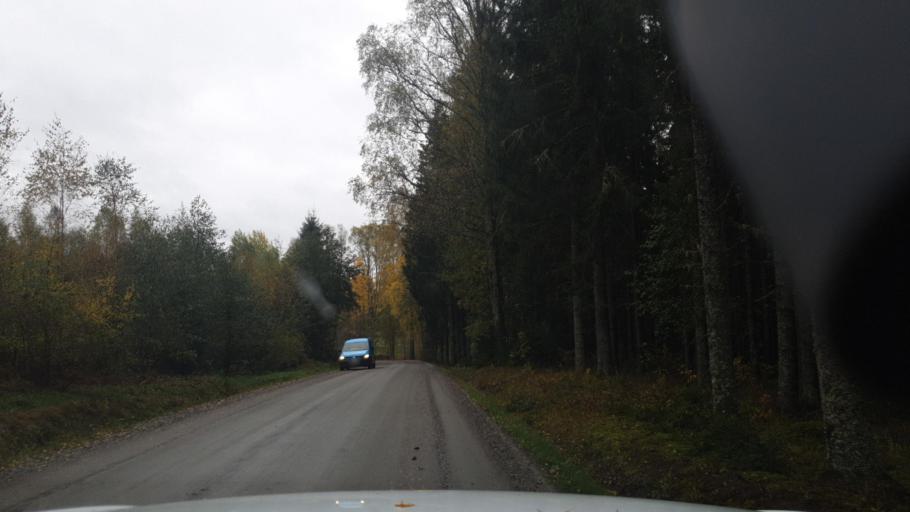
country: SE
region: Vaermland
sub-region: Karlstads Kommun
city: Edsvalla
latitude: 59.4877
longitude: 13.0354
